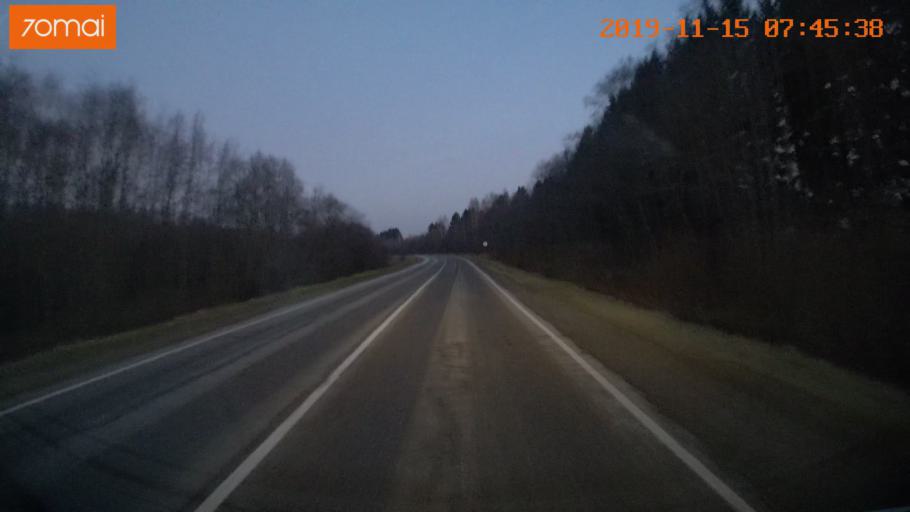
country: RU
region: Vologda
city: Sheksna
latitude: 58.8233
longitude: 38.2983
